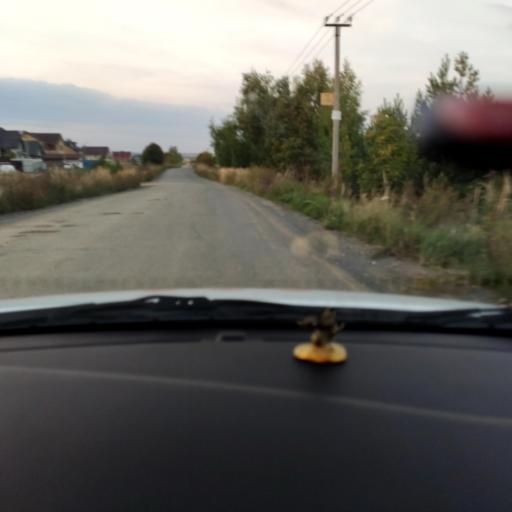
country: RU
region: Tatarstan
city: Vysokaya Gora
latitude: 55.8178
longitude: 49.3117
